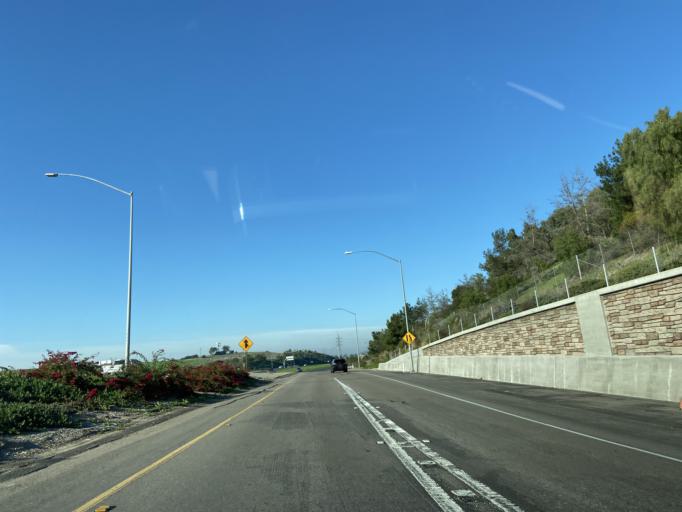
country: US
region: California
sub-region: San Diego County
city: Bonita
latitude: 32.6329
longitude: -116.9709
